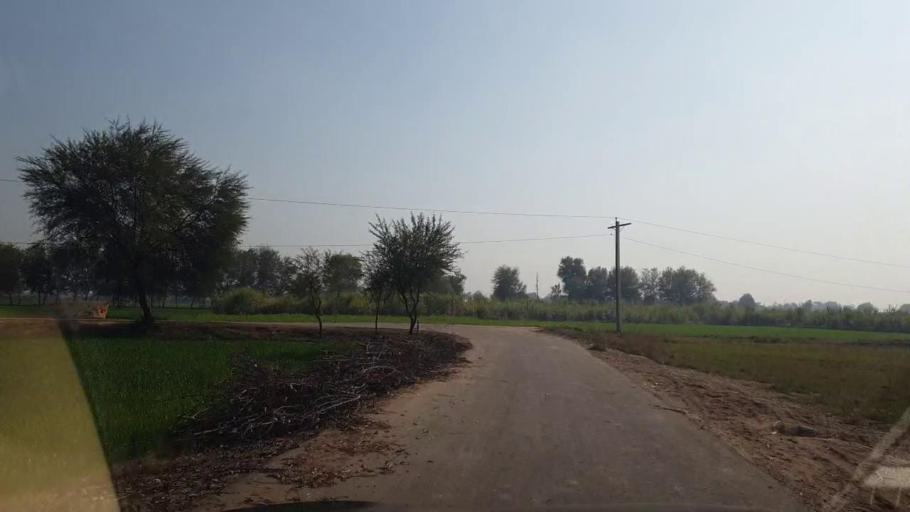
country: PK
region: Sindh
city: Ubauro
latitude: 28.1302
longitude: 69.7685
